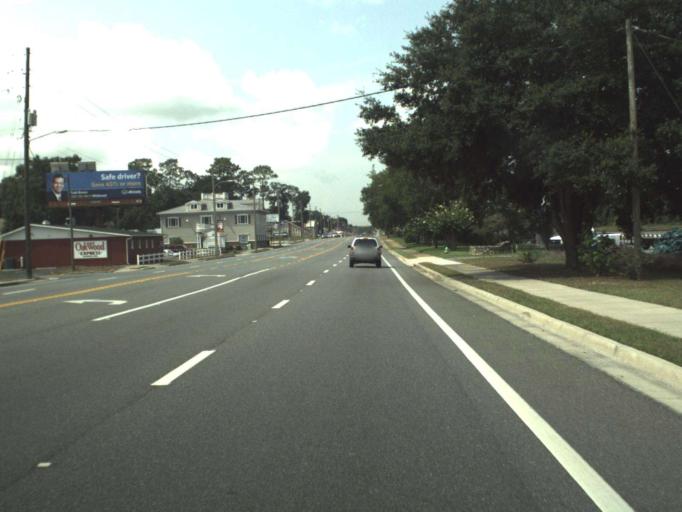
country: US
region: Florida
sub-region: Sumter County
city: Wildwood
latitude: 28.8707
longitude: -82.0373
